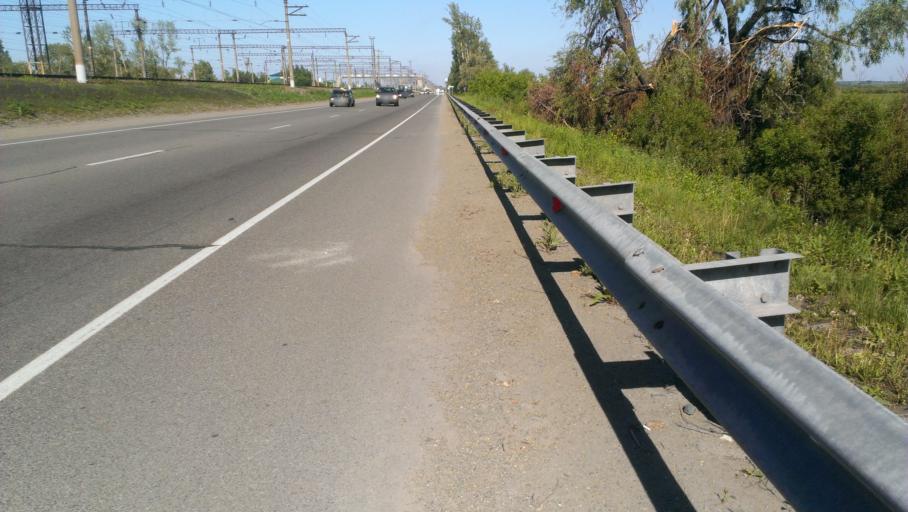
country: RU
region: Altai Krai
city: Novoaltaysk
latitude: 53.3702
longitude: 83.8677
